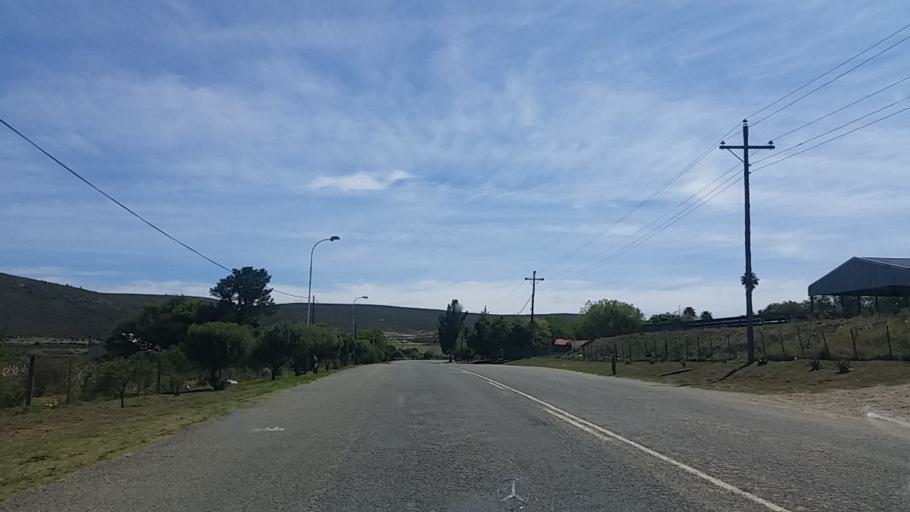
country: ZA
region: Western Cape
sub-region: Eden District Municipality
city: Knysna
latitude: -33.6517
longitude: 23.1347
